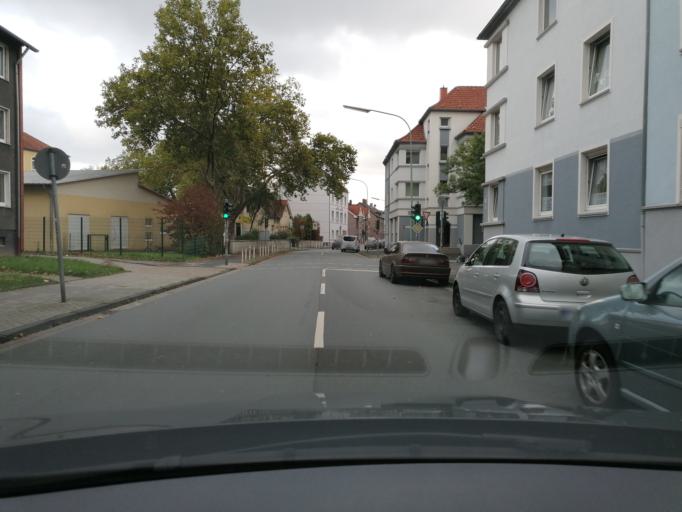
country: DE
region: North Rhine-Westphalia
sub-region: Regierungsbezirk Munster
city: Gelsenkirchen
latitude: 51.5380
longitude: 7.1524
